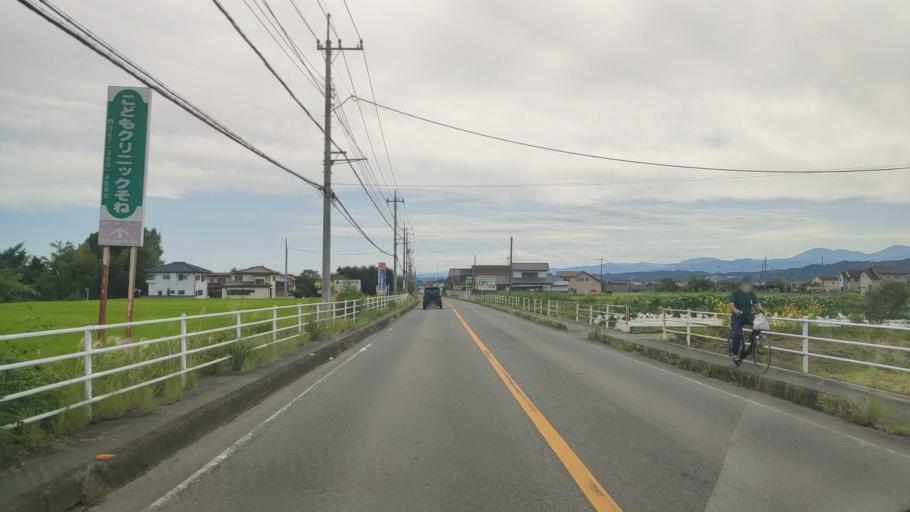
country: JP
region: Gunma
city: Kanekomachi
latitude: 36.3691
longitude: 138.9744
